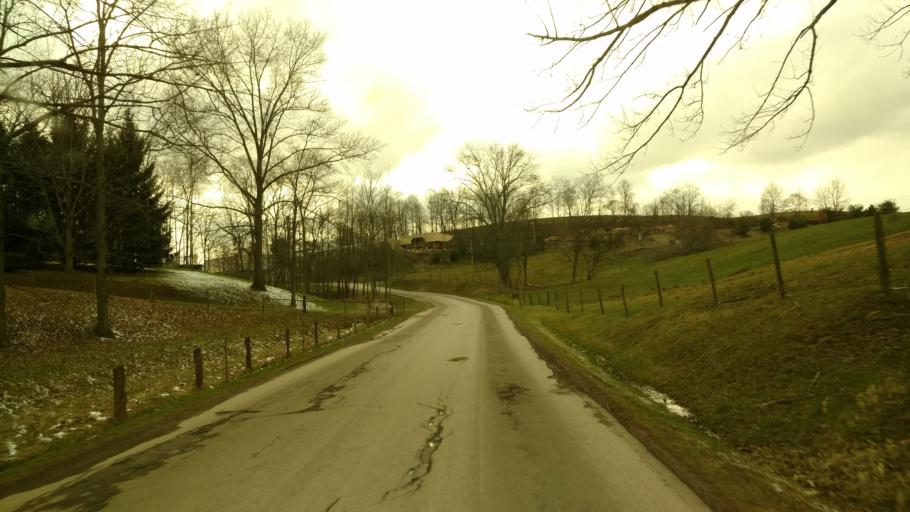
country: US
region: Ohio
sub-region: Tuscarawas County
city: Sugarcreek
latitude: 40.5066
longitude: -81.7583
